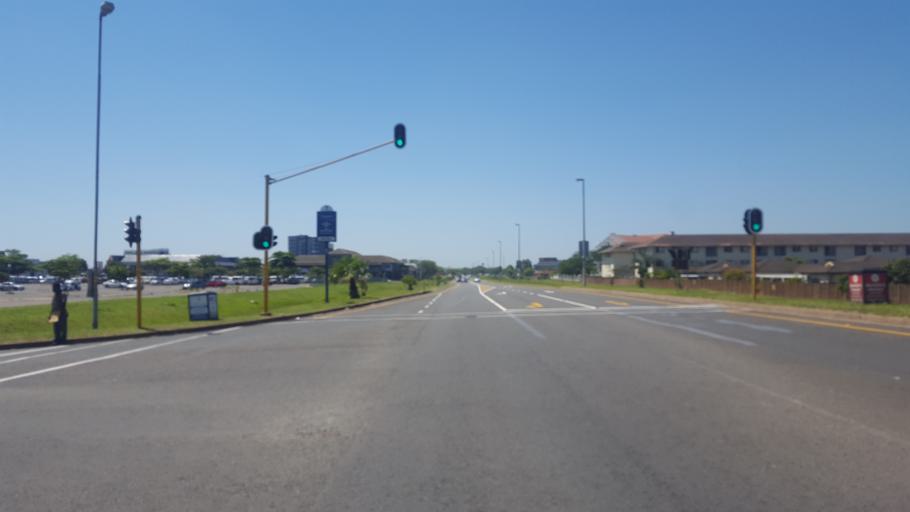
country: ZA
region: KwaZulu-Natal
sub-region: uThungulu District Municipality
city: Richards Bay
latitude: -28.7558
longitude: 32.0530
